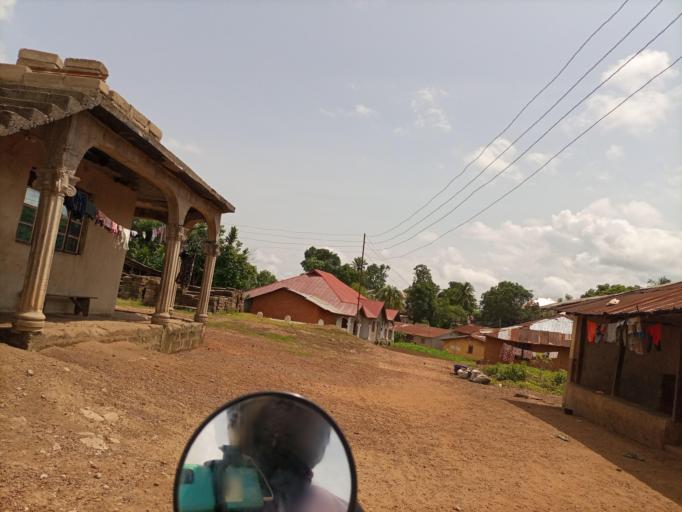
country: SL
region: Southern Province
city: Bo
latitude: 7.9733
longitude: -11.7622
